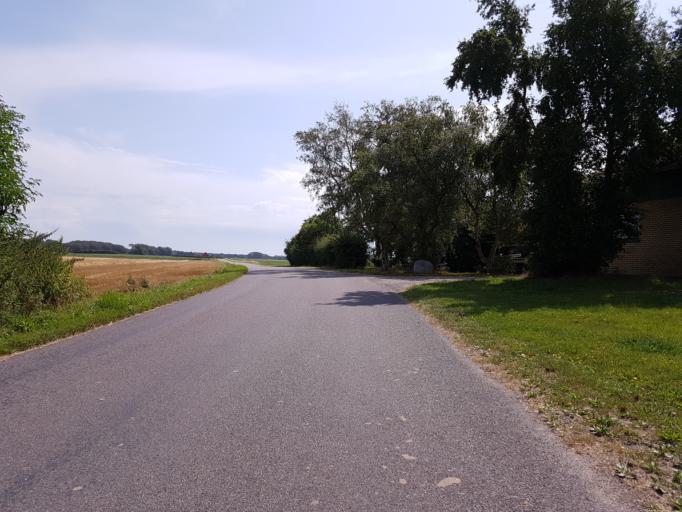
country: DK
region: Zealand
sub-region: Guldborgsund Kommune
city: Nykobing Falster
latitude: 54.5981
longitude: 11.9424
